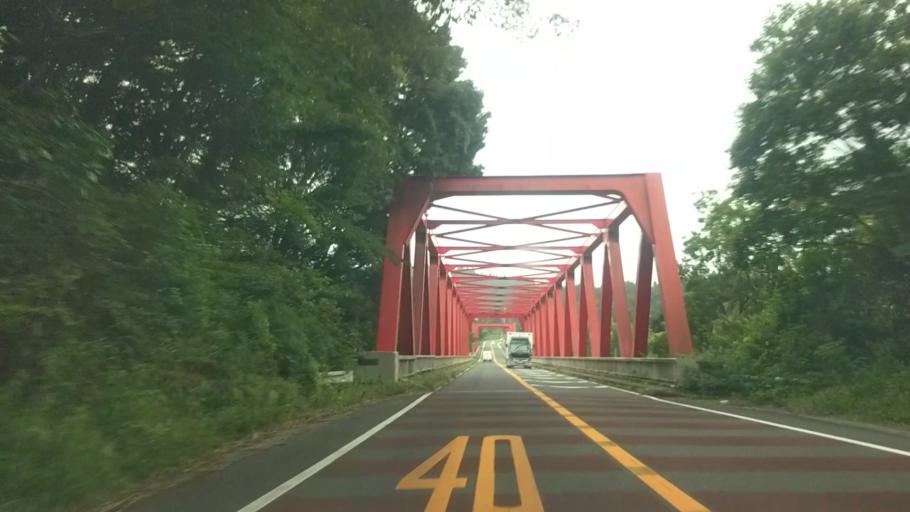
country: JP
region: Chiba
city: Kawaguchi
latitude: 35.2223
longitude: 140.0719
